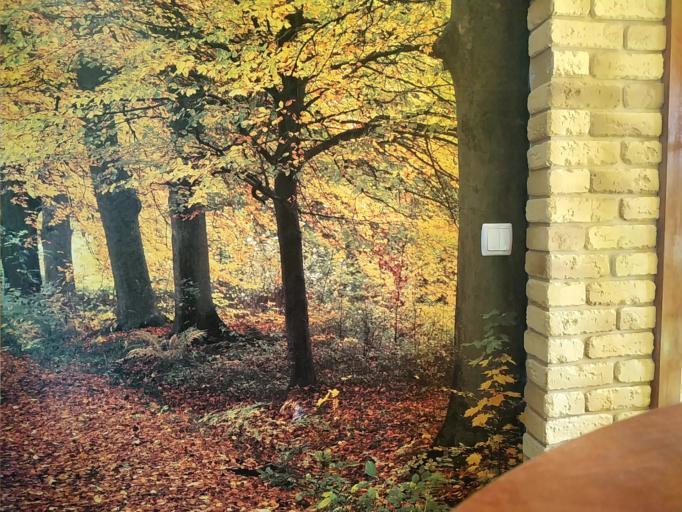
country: RU
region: Vologda
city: Molochnoye
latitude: 58.9669
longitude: 39.6350
